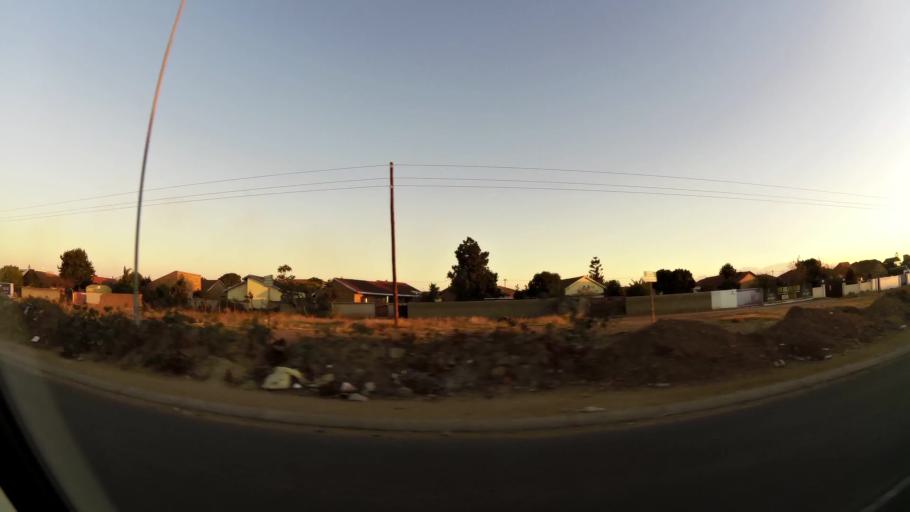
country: ZA
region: Limpopo
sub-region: Capricorn District Municipality
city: Polokwane
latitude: -23.8536
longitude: 29.3755
